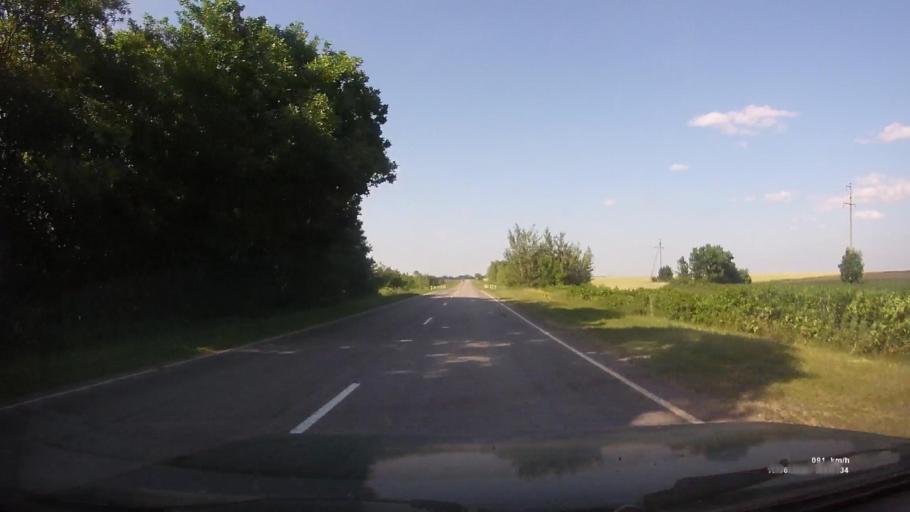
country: RU
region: Rostov
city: Kazanskaya
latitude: 49.9086
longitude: 41.3146
